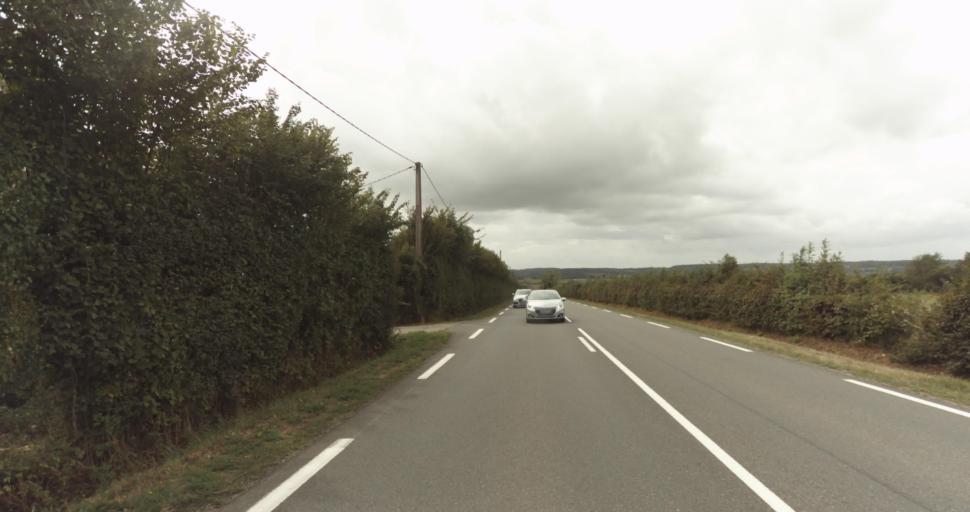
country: FR
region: Lower Normandy
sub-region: Departement de l'Orne
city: Gace
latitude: 48.8160
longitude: 0.3144
